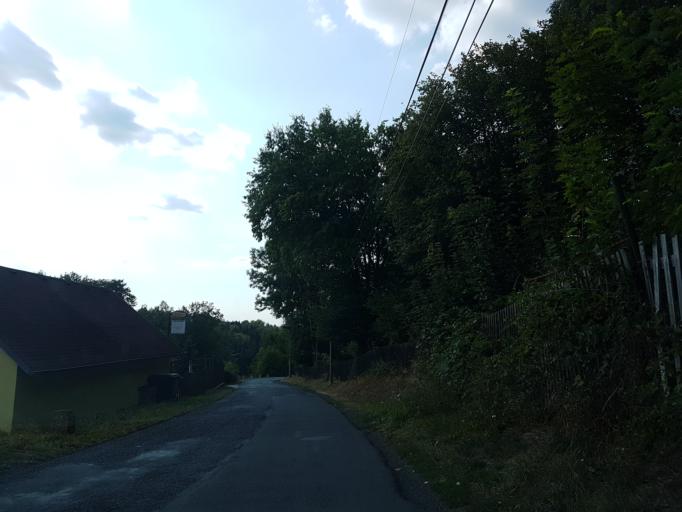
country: CZ
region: Ustecky
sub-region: Okres Decin
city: Decin
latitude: 50.8613
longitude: 14.2646
